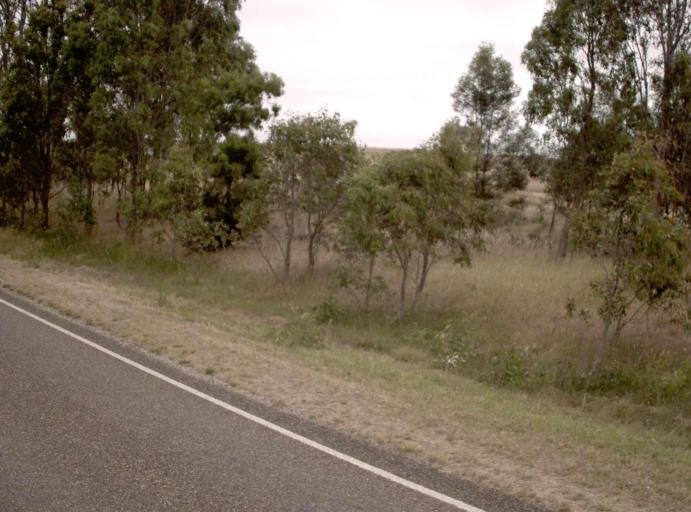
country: AU
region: Victoria
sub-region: Wellington
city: Heyfield
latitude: -38.1356
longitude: 146.7918
